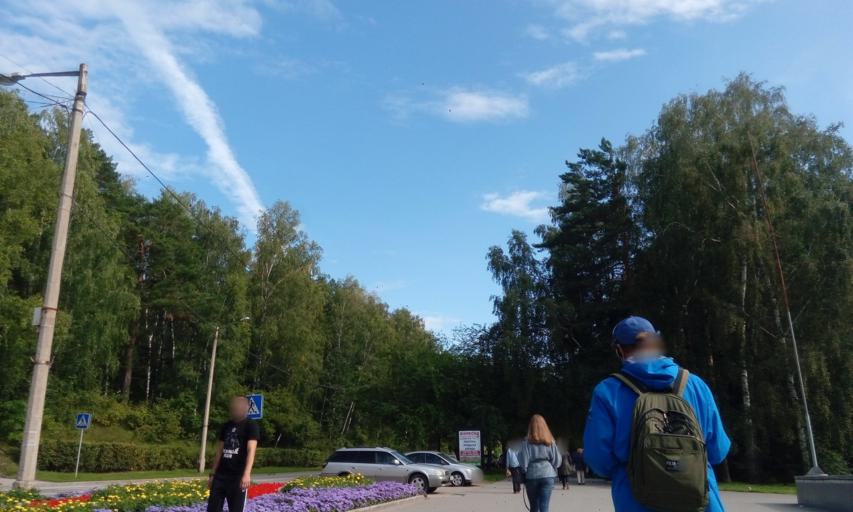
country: RU
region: Novosibirsk
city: Akademgorodok
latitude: 54.8383
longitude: 83.0974
